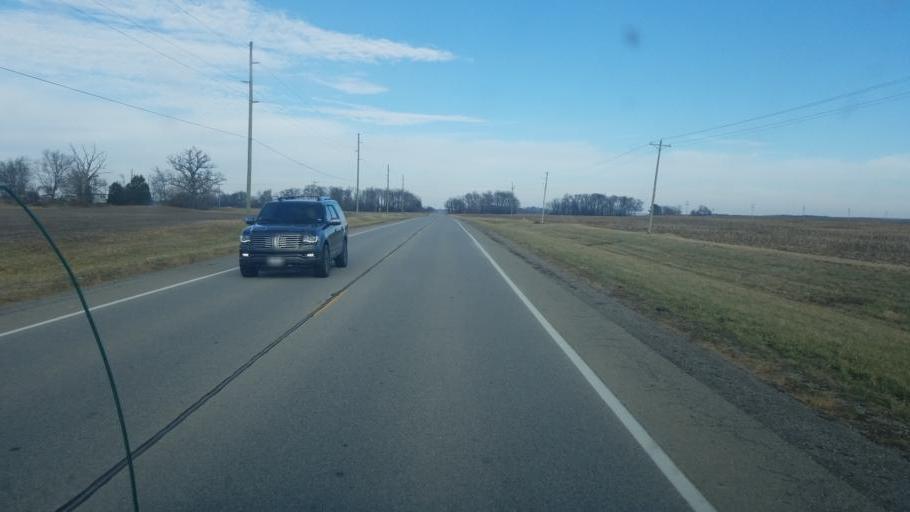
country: US
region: Illinois
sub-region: White County
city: Carmi
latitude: 38.1161
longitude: -88.1154
